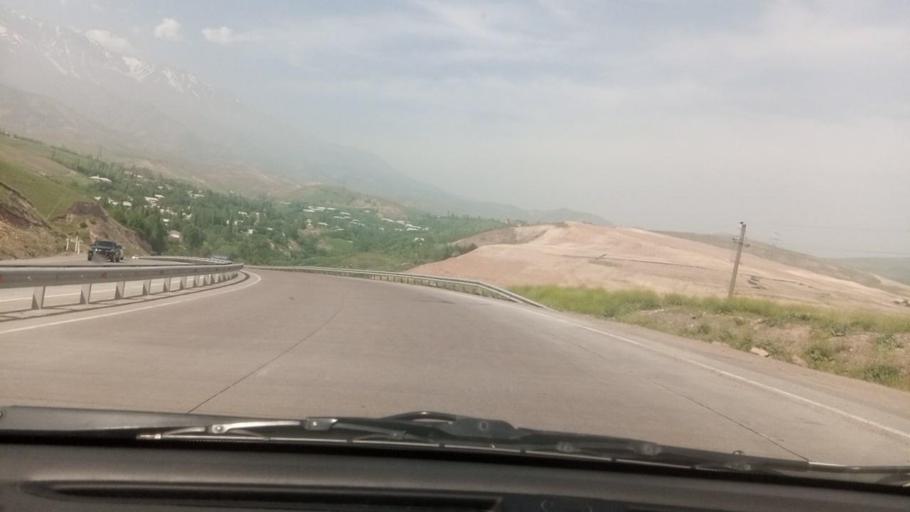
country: UZ
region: Toshkent
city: Angren
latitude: 41.0683
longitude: 70.2322
